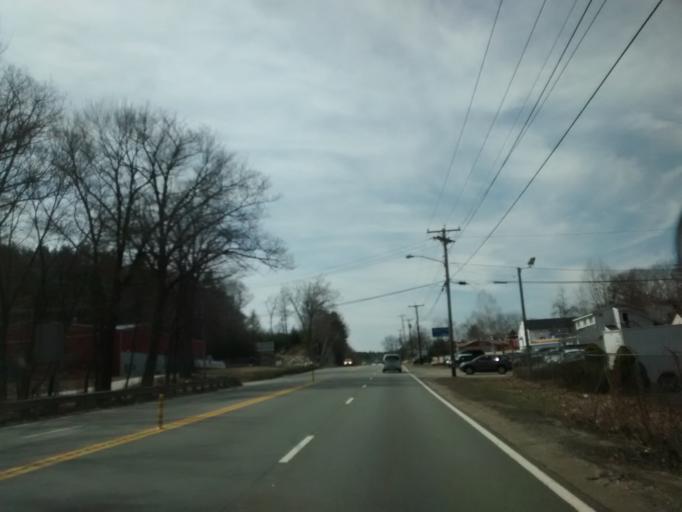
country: US
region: Massachusetts
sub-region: Worcester County
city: Charlton
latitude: 42.1543
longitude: -71.9137
